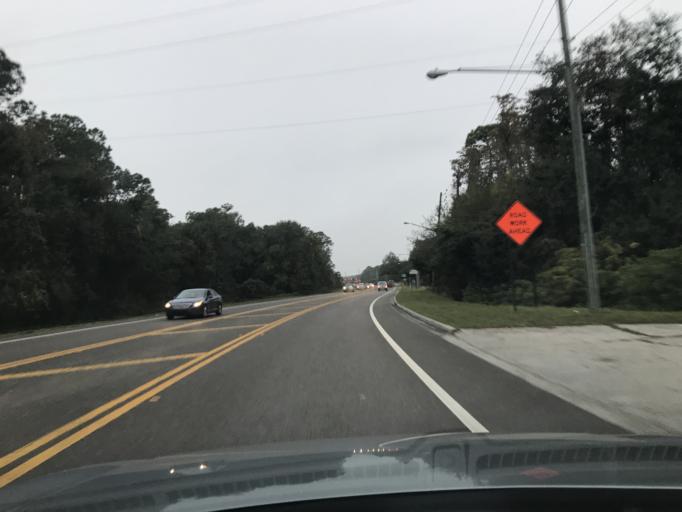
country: US
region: Florida
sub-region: Pinellas County
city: Oldsmar
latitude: 28.0558
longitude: -82.6437
